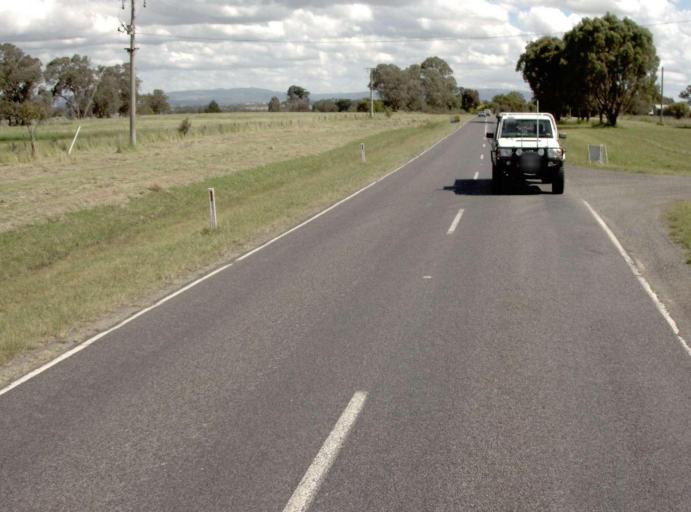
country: AU
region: Victoria
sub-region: Latrobe
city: Traralgon
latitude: -38.1476
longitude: 146.5235
